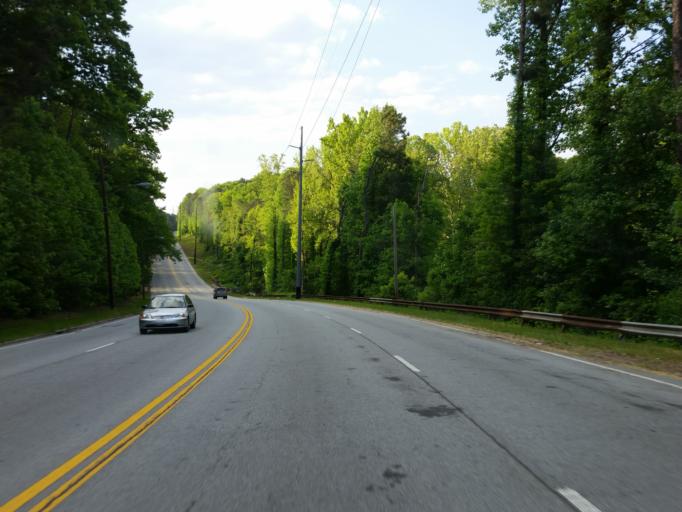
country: US
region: Georgia
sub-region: Cobb County
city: Vinings
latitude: 33.7928
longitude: -84.4740
